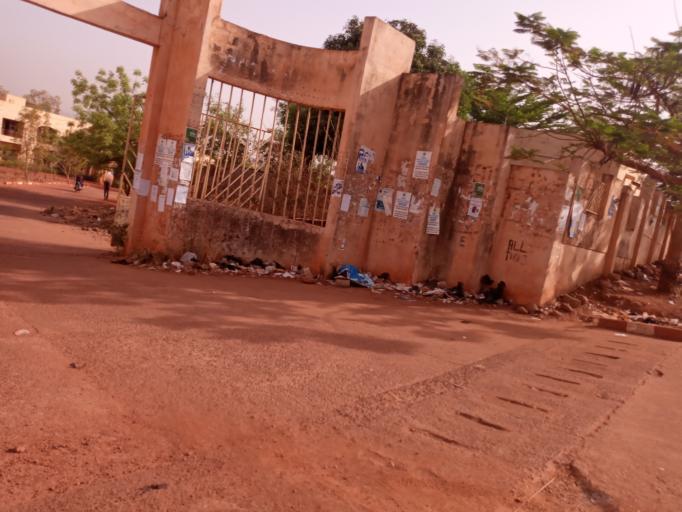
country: ML
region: Bamako
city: Bamako
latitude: 12.6122
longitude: -7.9912
